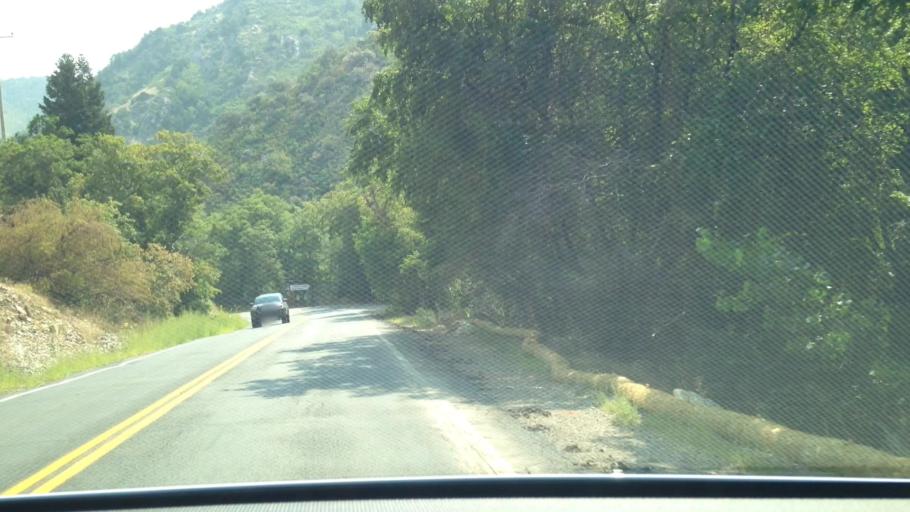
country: US
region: Utah
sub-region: Salt Lake County
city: Mount Olympus
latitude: 40.6909
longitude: -111.7653
